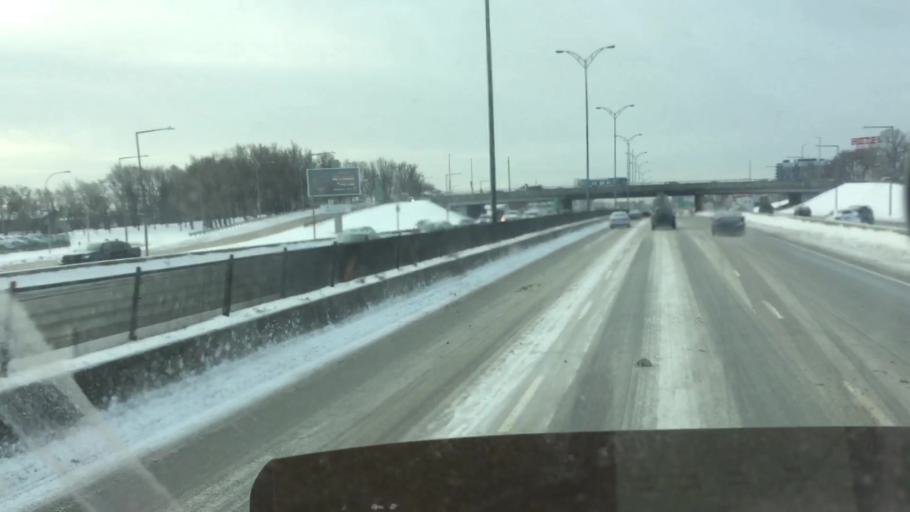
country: CA
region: Quebec
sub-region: Montreal
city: Saint-Leonard
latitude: 45.5840
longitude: -73.5876
